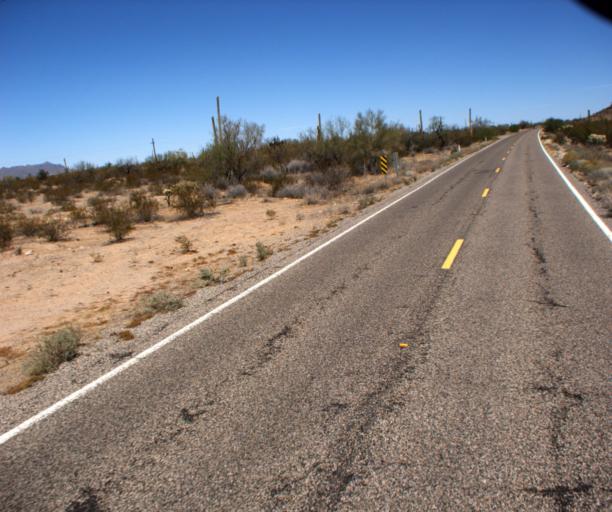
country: US
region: Arizona
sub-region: Pima County
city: Ajo
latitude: 32.2188
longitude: -112.7572
